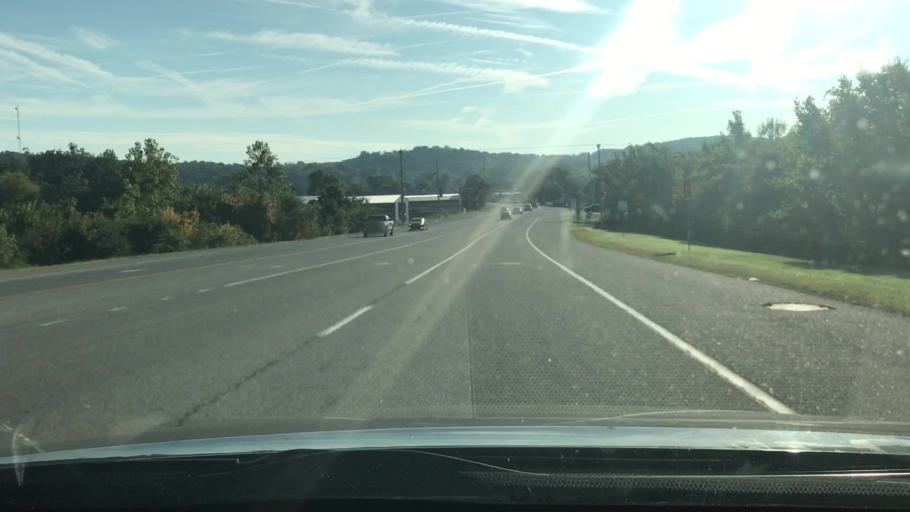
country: US
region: Tennessee
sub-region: Cheatham County
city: Ashland City
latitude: 36.2719
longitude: -87.0716
